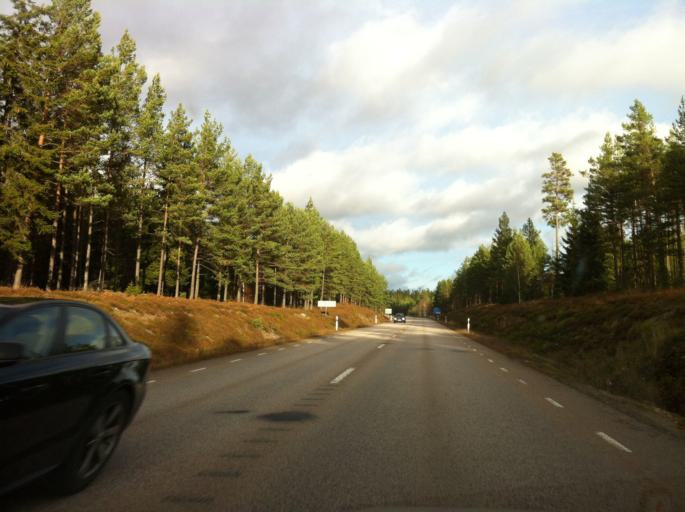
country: SE
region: Kronoberg
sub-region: Vaxjo Kommun
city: Braas
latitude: 57.0820
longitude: 15.1746
